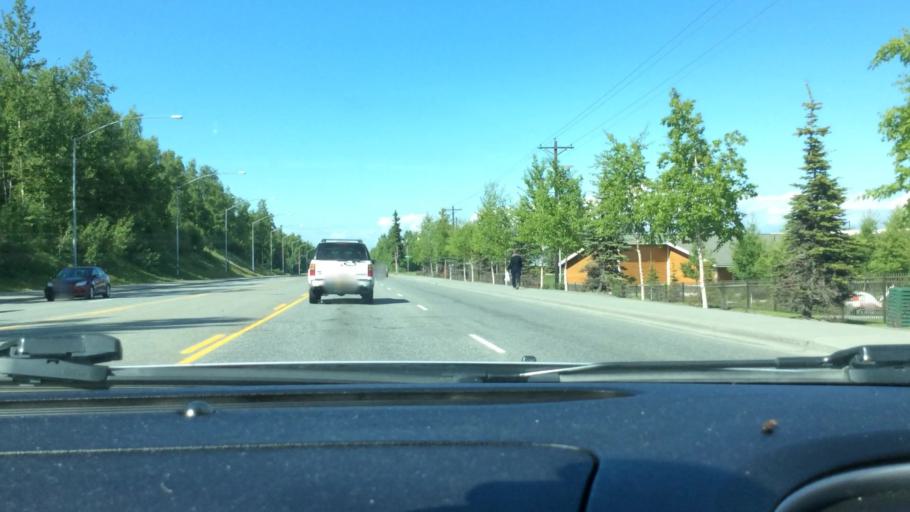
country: US
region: Alaska
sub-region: Anchorage Municipality
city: Anchorage
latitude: 61.2118
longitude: -149.7780
